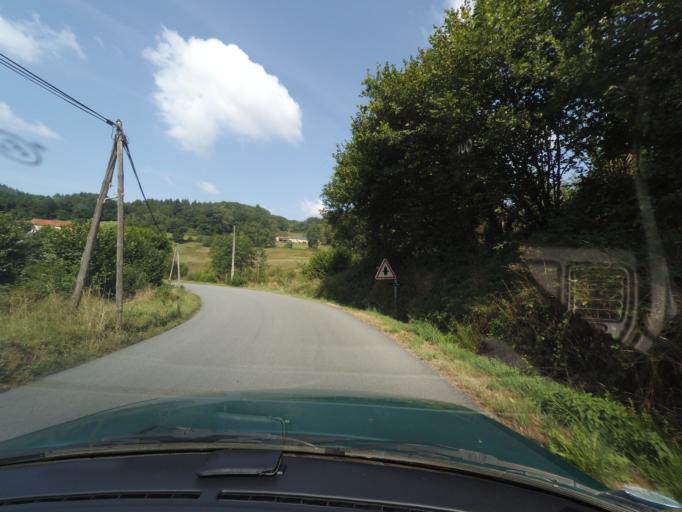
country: FR
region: Limousin
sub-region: Departement de la Correze
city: Bugeat
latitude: 45.7346
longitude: 1.8908
